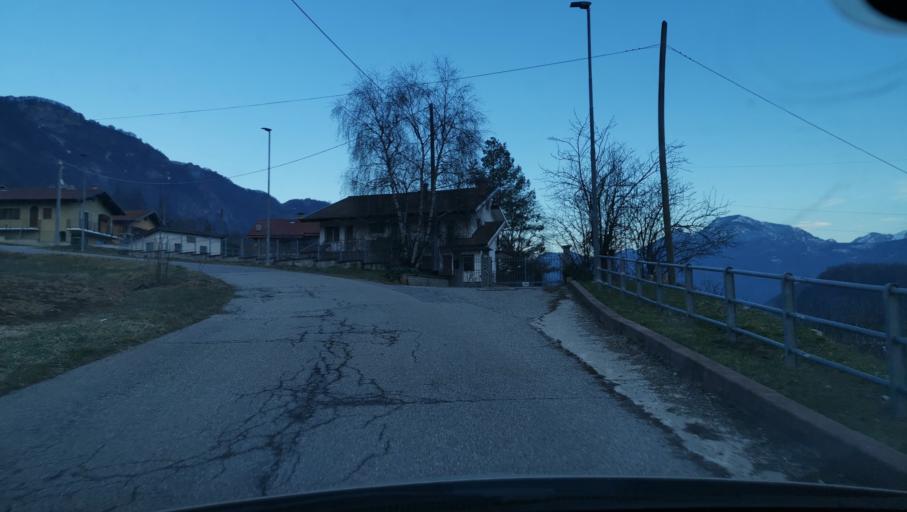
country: IT
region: Piedmont
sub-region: Provincia di Cuneo
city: Demonte
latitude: 44.3200
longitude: 7.2954
